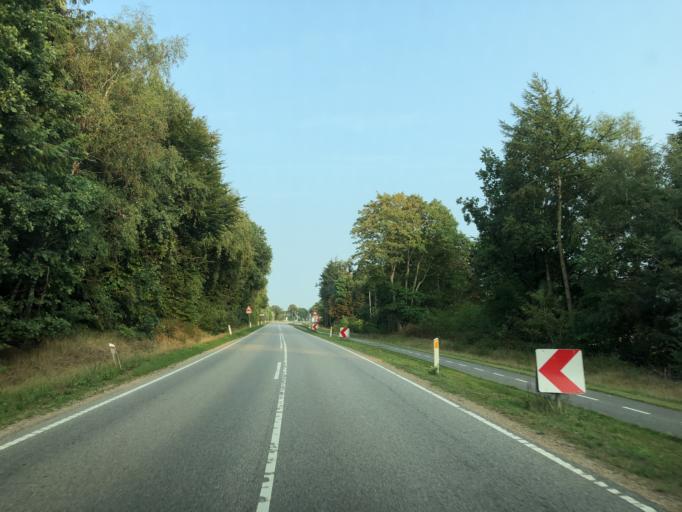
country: DK
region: South Denmark
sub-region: Billund Kommune
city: Grindsted
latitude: 55.8173
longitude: 9.0142
